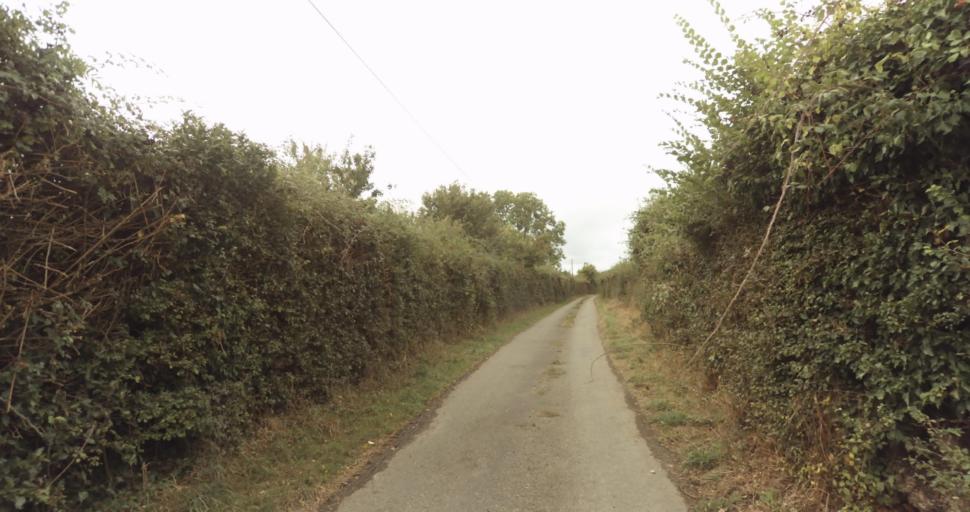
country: FR
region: Lower Normandy
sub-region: Departement de l'Orne
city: Gace
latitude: 48.8318
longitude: 0.3051
